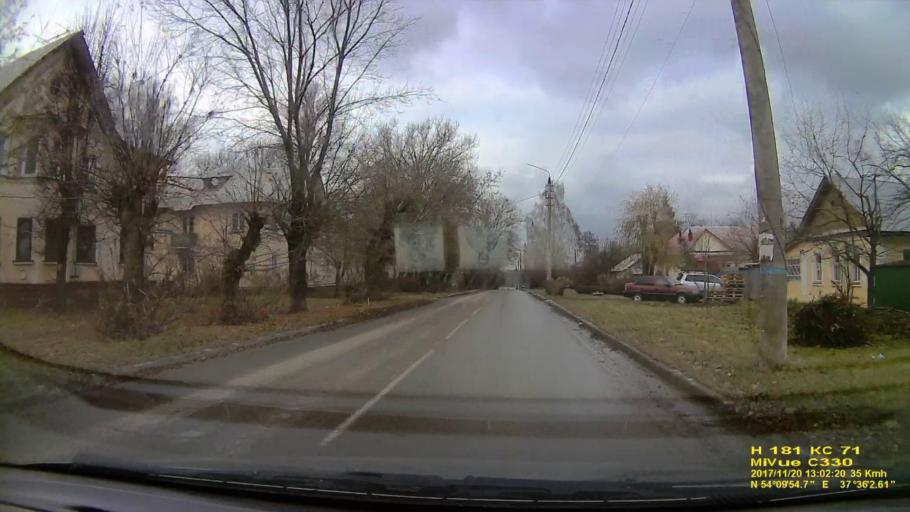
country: RU
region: Tula
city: Mendeleyevskiy
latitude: 54.1653
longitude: 37.6008
